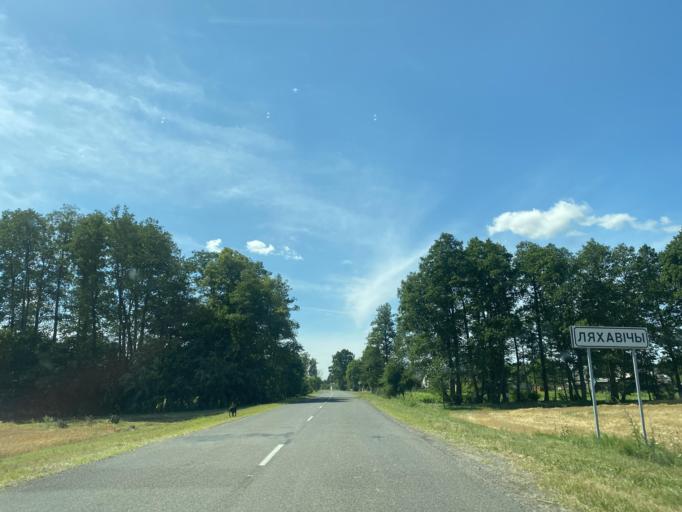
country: BY
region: Brest
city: Ivanava
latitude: 52.1912
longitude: 25.6108
